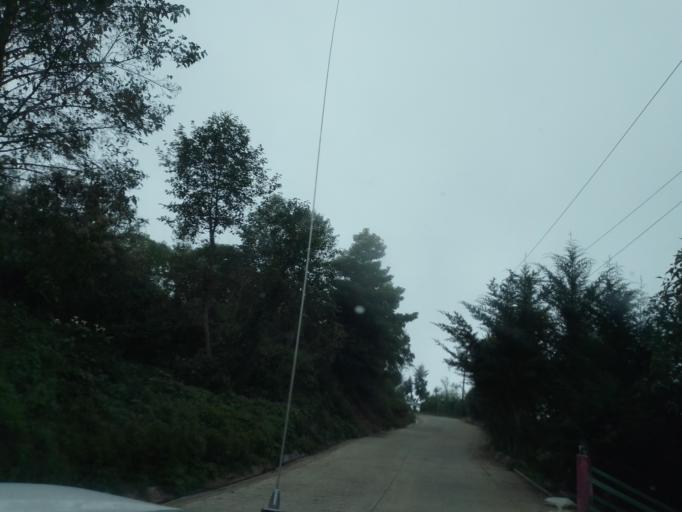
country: MX
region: Chiapas
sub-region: Union Juarez
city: Santo Domingo
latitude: 15.0879
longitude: -92.0912
